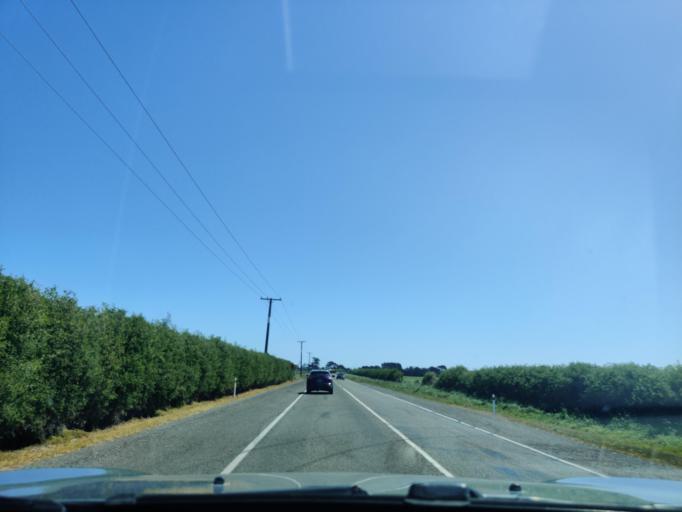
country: NZ
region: Taranaki
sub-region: South Taranaki District
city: Hawera
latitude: -39.5463
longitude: 174.0816
